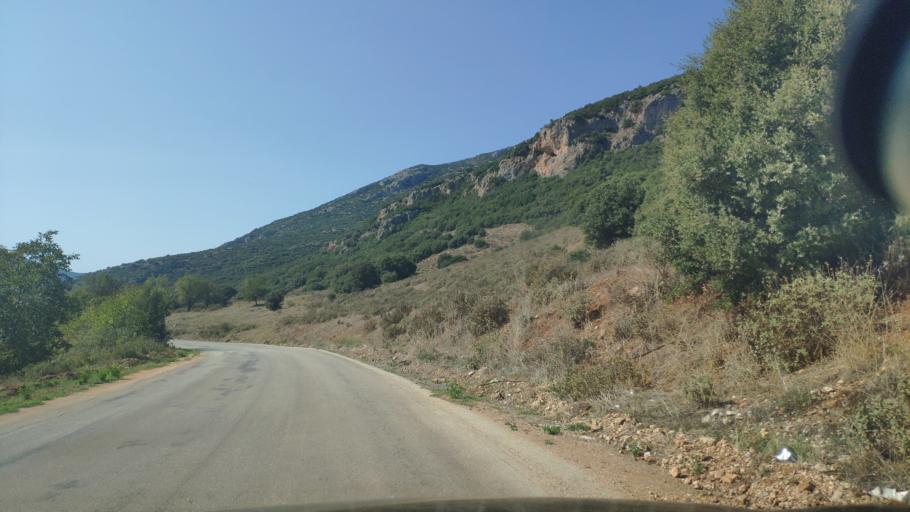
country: GR
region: Peloponnese
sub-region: Nomos Korinthias
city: Nemea
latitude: 37.9124
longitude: 22.5260
